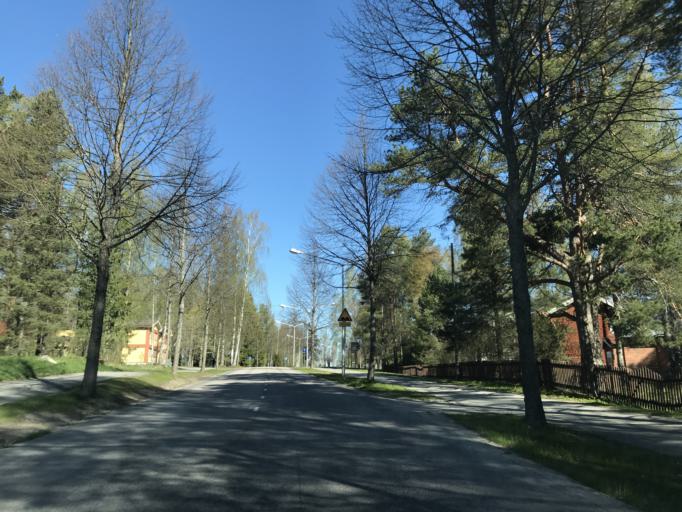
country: FI
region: Paijanne Tavastia
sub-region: Lahti
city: Orimattila
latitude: 60.8082
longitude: 25.7383
